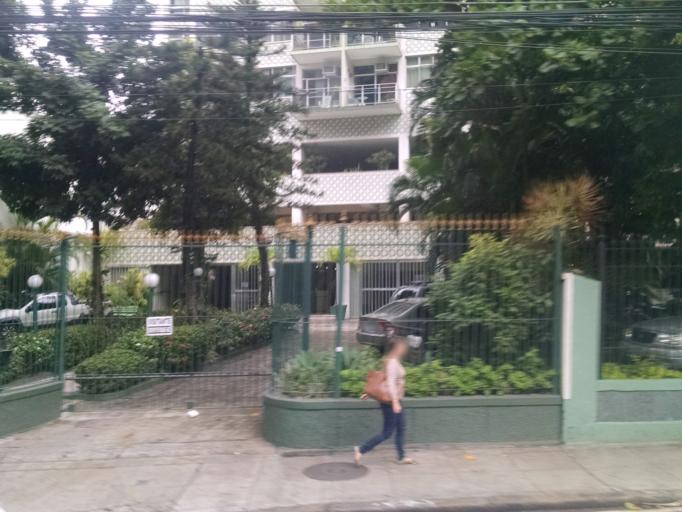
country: BR
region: Rio de Janeiro
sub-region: Rio De Janeiro
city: Rio de Janeiro
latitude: -22.9518
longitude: -43.1953
